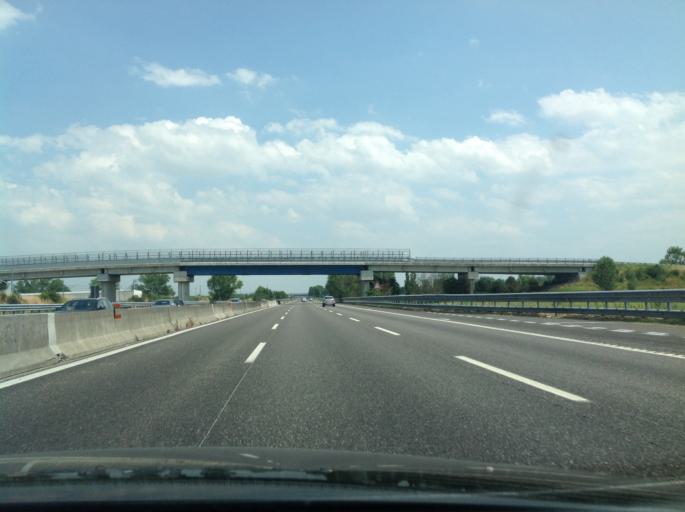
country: IT
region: Emilia-Romagna
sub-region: Provincia di Parma
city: Fontanellato
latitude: 44.8808
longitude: 10.1445
